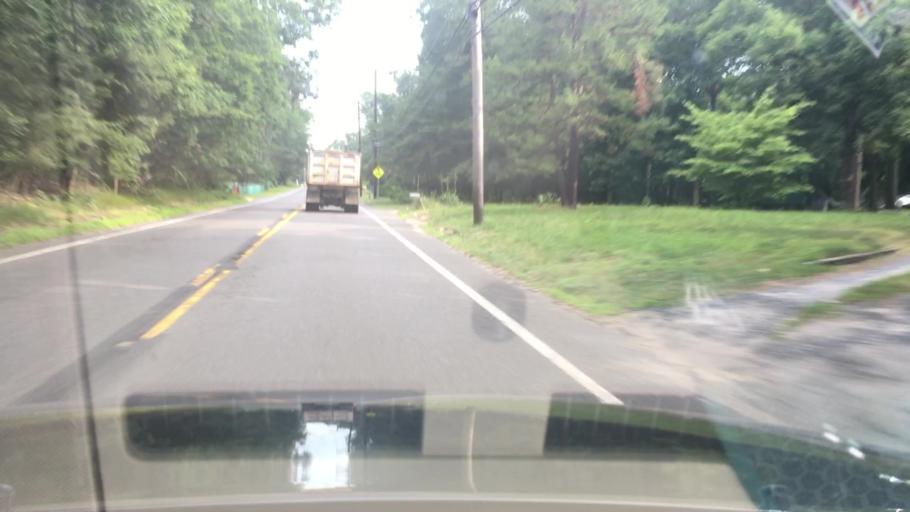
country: US
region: New Jersey
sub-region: Ocean County
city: Vista Center
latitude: 40.1197
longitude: -74.3928
